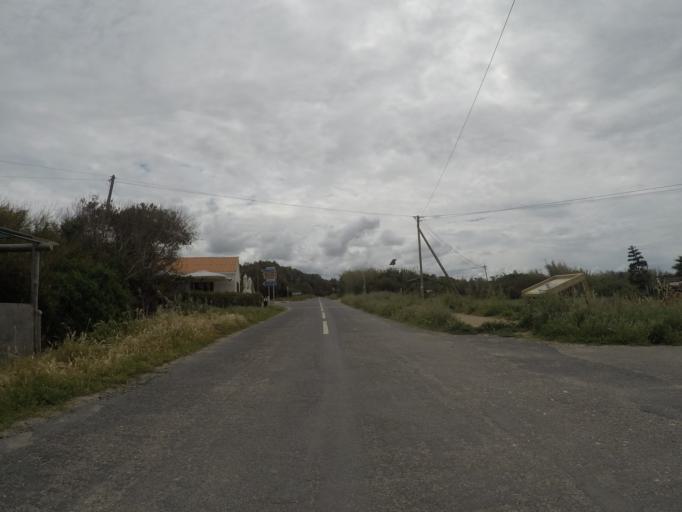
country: PT
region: Beja
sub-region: Odemira
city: Sao Teotonio
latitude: 37.5497
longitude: -8.7919
